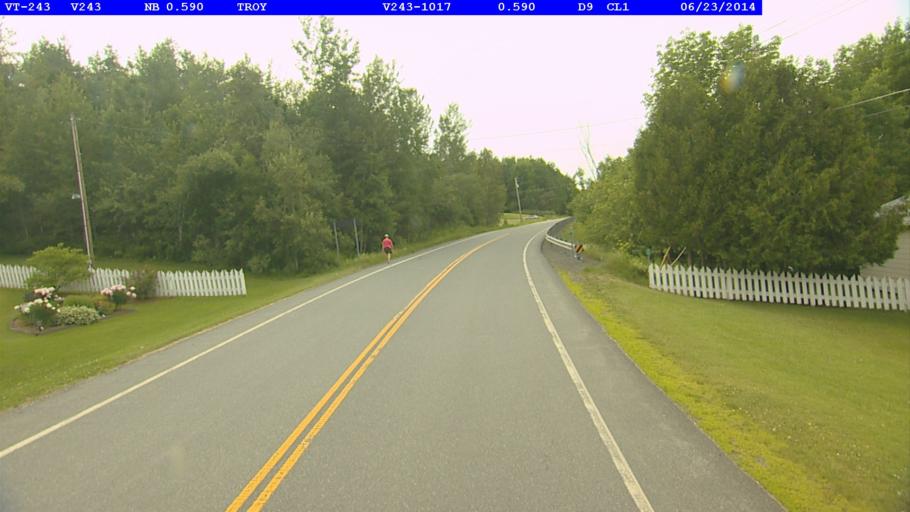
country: US
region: Vermont
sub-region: Orleans County
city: Newport
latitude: 44.9993
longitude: -72.4110
